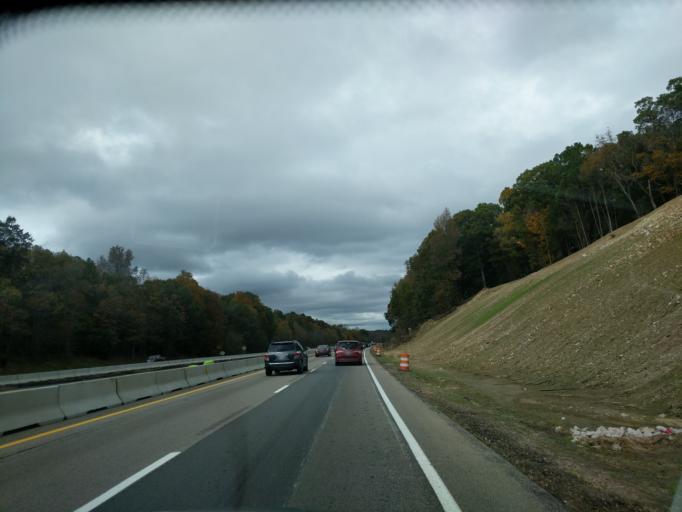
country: US
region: North Carolina
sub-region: Rowan County
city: Landis
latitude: 35.5137
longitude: -80.5676
